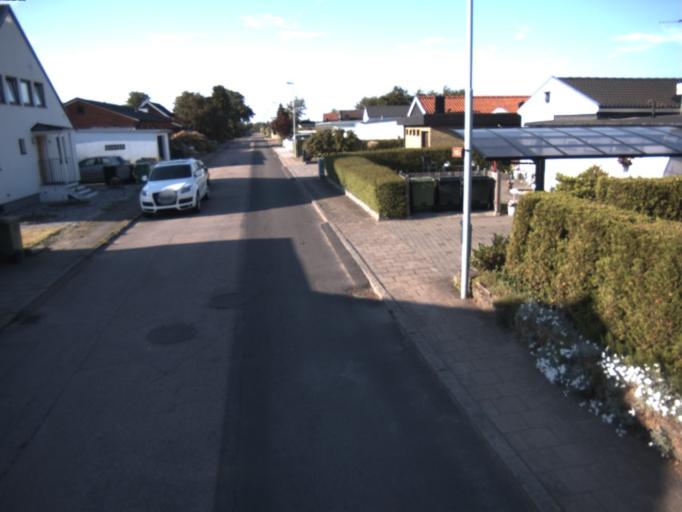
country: SE
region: Skane
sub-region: Helsingborg
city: Helsingborg
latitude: 56.0418
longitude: 12.7335
